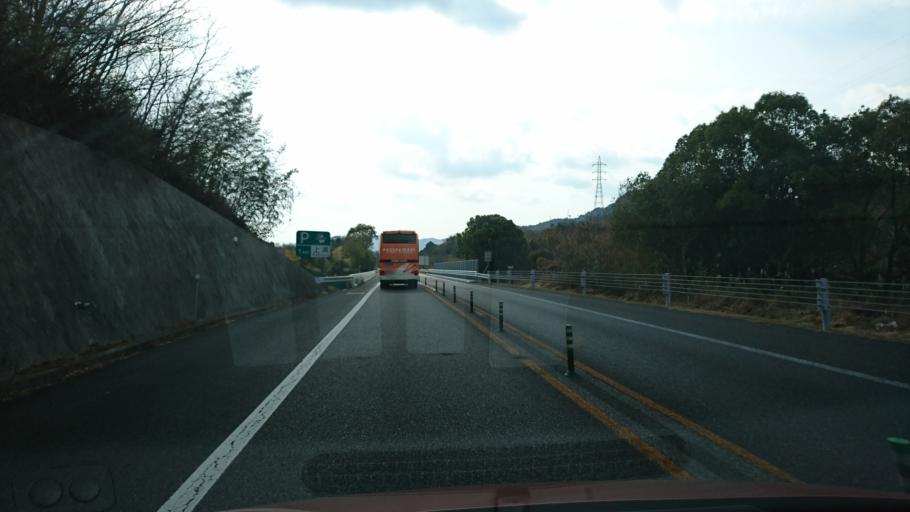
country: JP
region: Hiroshima
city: Innoshima
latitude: 34.2409
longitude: 133.0479
